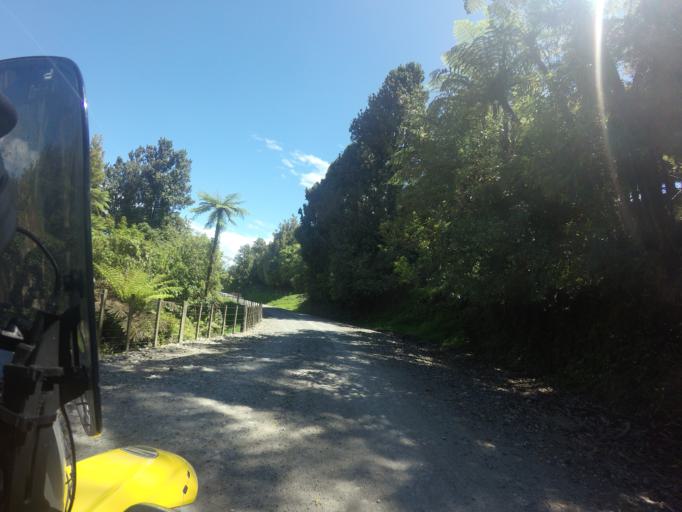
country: NZ
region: Hawke's Bay
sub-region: Wairoa District
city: Wairoa
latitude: -38.9667
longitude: 177.7069
